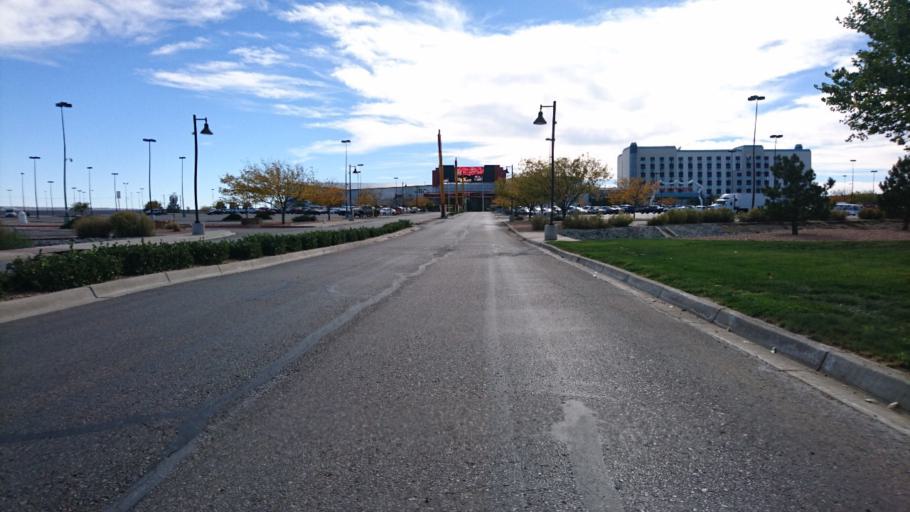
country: US
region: New Mexico
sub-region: Bernalillo County
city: South Valley
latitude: 35.0302
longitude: -106.9510
